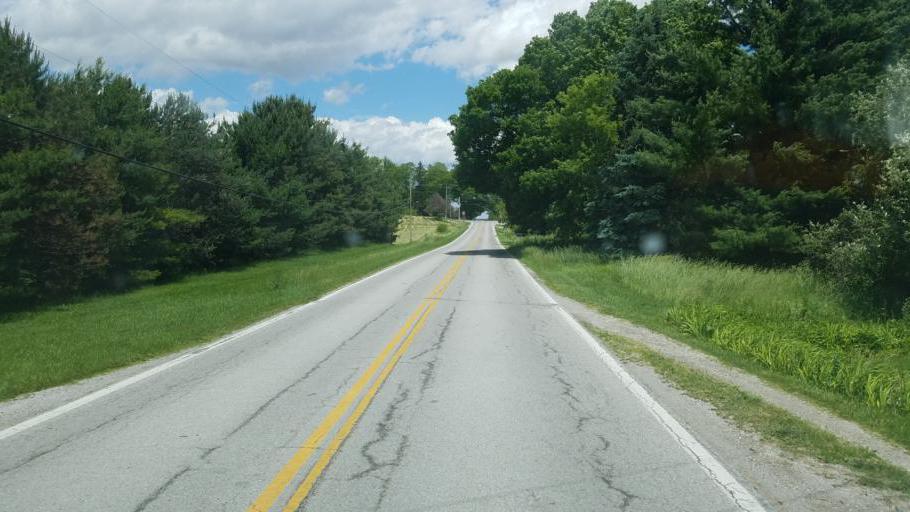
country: US
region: Ohio
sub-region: Huron County
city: Willard
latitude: 41.1028
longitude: -82.6856
